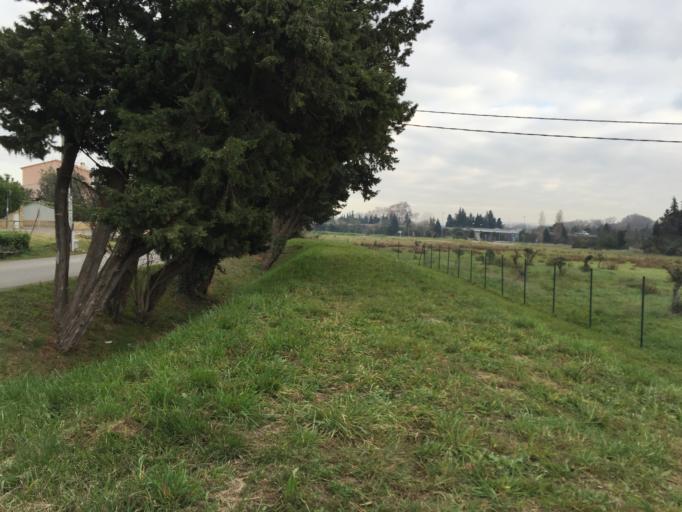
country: FR
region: Provence-Alpes-Cote d'Azur
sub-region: Departement du Vaucluse
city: Sorgues
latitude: 44.0118
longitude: 4.8614
